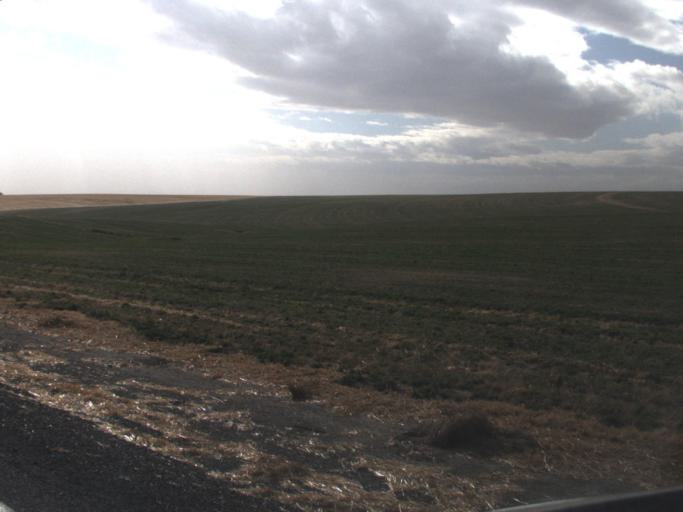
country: US
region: Washington
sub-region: Okanogan County
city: Coulee Dam
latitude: 47.5019
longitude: -118.7849
